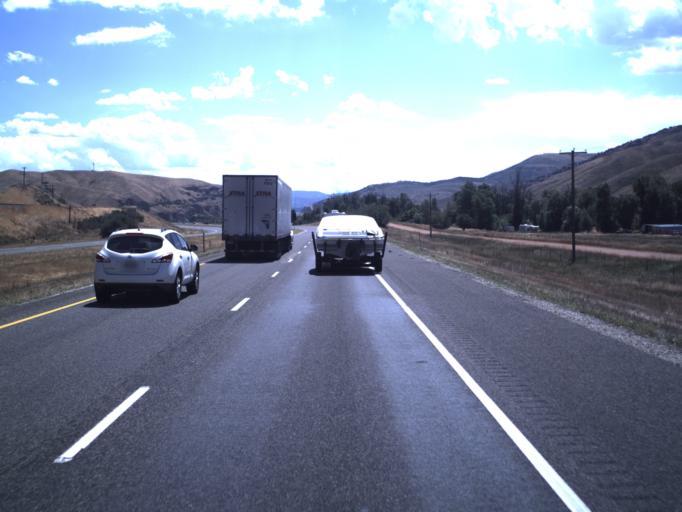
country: US
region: Utah
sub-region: Summit County
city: Coalville
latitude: 40.9974
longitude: -111.4658
